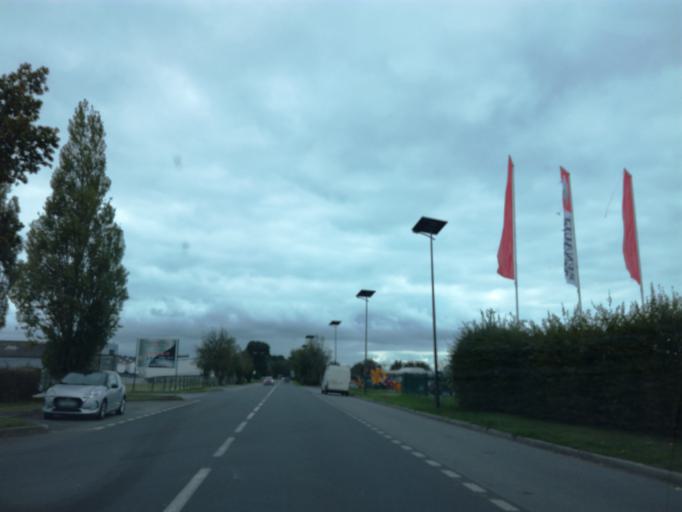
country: FR
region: Brittany
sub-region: Departement des Cotes-d'Armor
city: Loudeac
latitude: 48.1560
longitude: -2.7576
